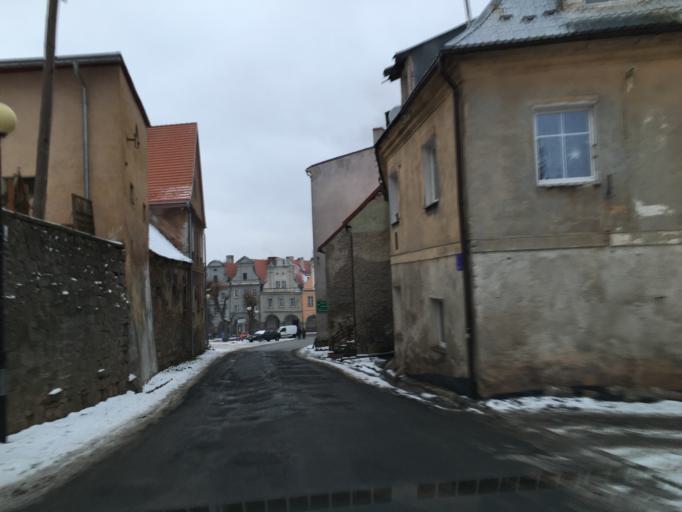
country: PL
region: Lower Silesian Voivodeship
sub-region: Powiat kamiennogorski
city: Krzeszow
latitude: 50.6653
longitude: 16.0698
